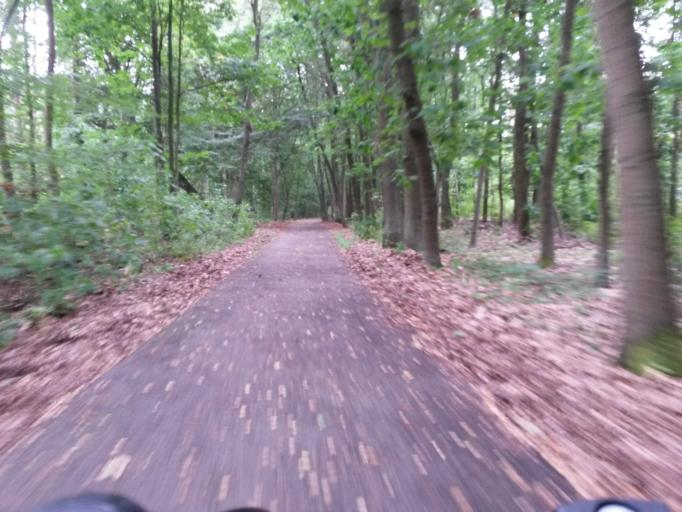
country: DE
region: Brandenburg
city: Templin
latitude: 53.1288
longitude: 13.5388
